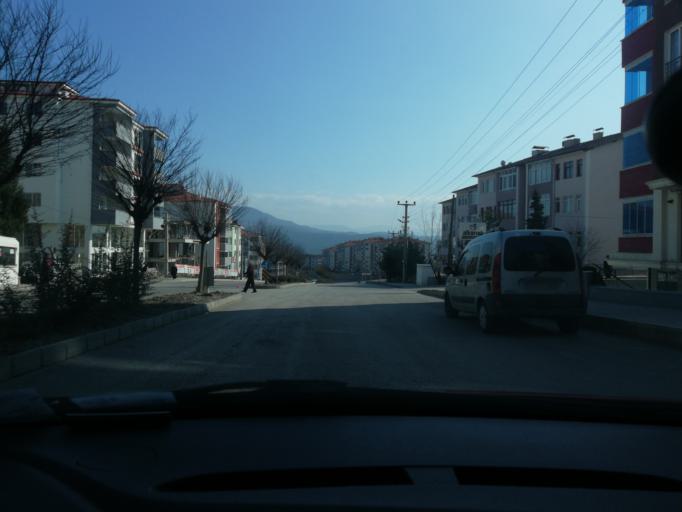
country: TR
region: Karabuk
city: Safranbolu
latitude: 41.2383
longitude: 32.6642
